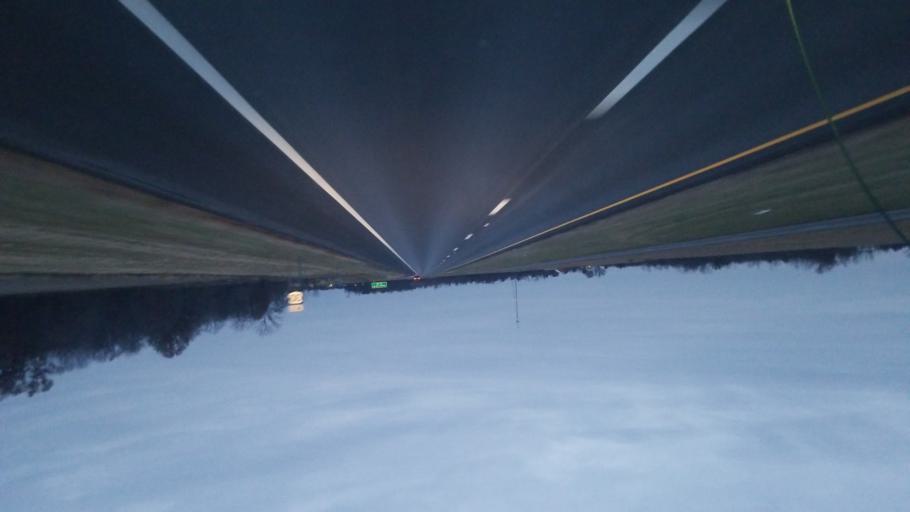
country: US
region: Ohio
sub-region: Hardin County
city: Forest
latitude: 40.8249
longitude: -83.4655
